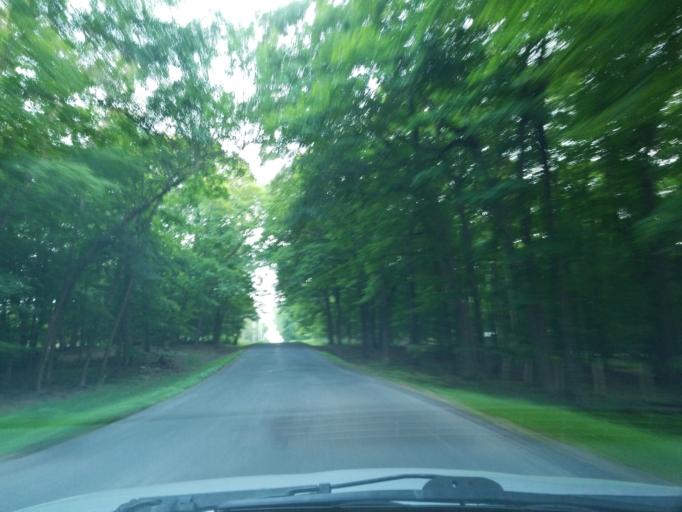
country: US
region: Minnesota
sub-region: Washington County
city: Stillwater
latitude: 45.0873
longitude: -92.7713
